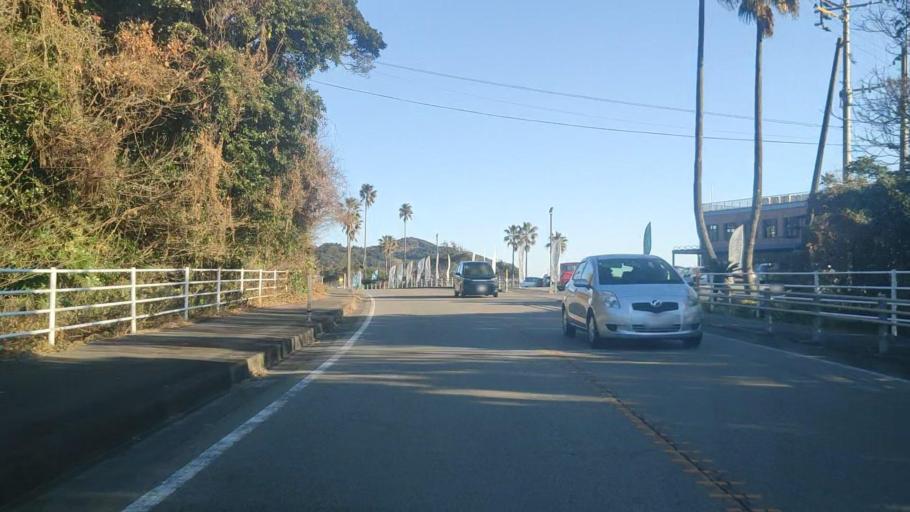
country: JP
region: Miyazaki
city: Nobeoka
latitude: 32.3581
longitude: 131.6217
